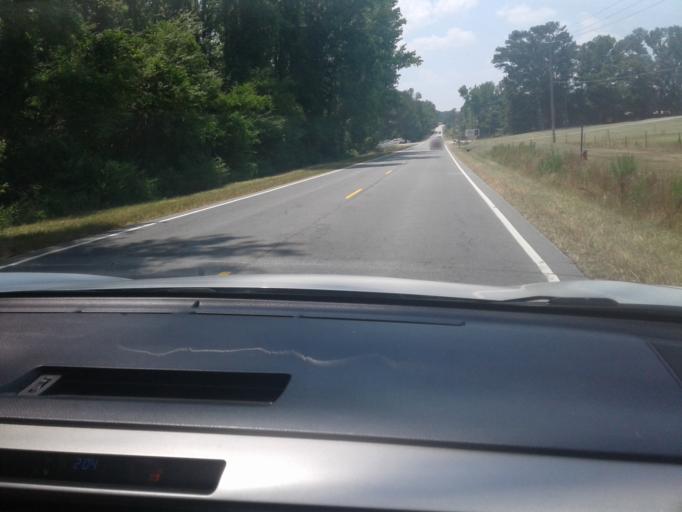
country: US
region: North Carolina
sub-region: Johnston County
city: Benson
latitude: 35.3885
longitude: -78.5703
